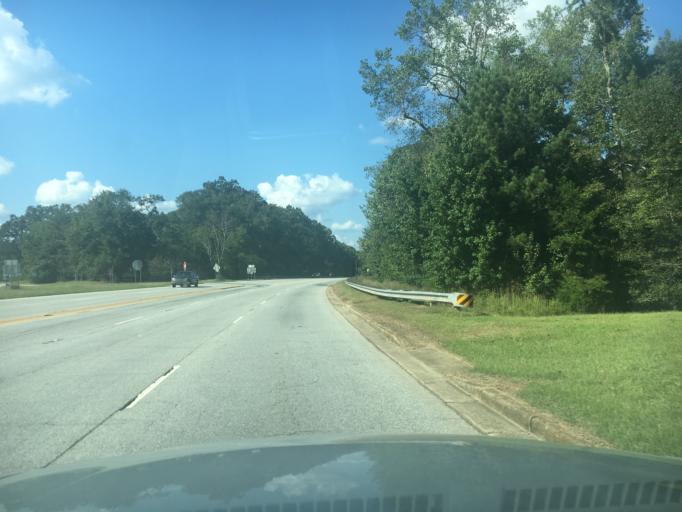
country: US
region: South Carolina
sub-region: Greenwood County
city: Ware Shoals
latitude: 34.3777
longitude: -82.2245
